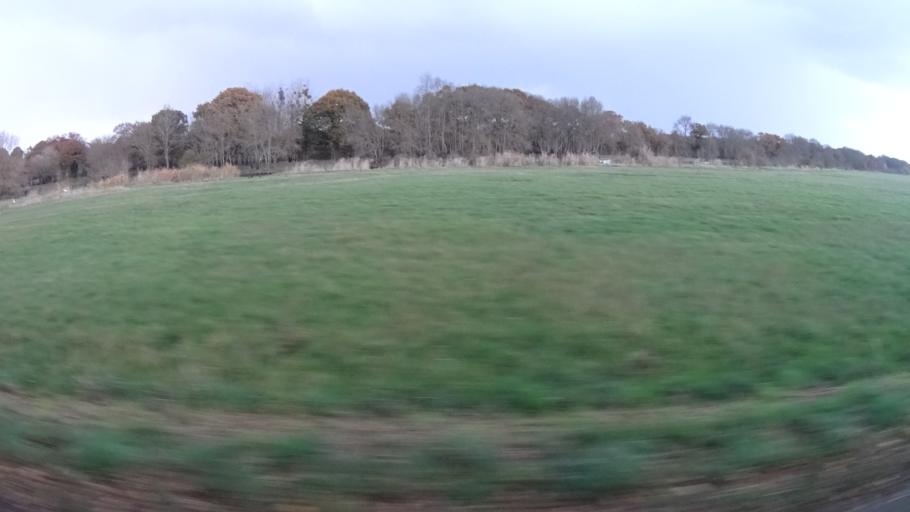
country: FR
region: Brittany
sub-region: Departement d'Ille-et-Vilaine
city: Sainte-Marie
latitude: 47.6706
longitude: -2.0333
